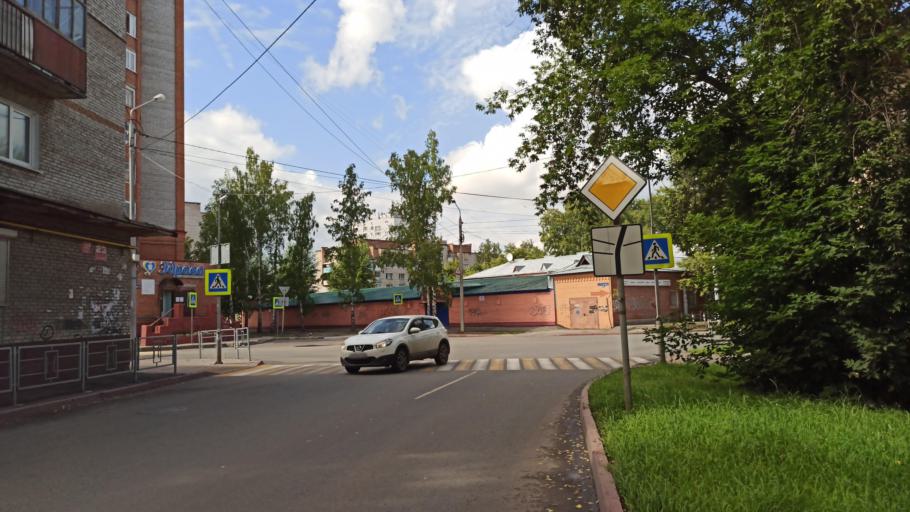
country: RU
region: Tomsk
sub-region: Tomskiy Rayon
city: Tomsk
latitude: 56.4606
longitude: 84.9821
